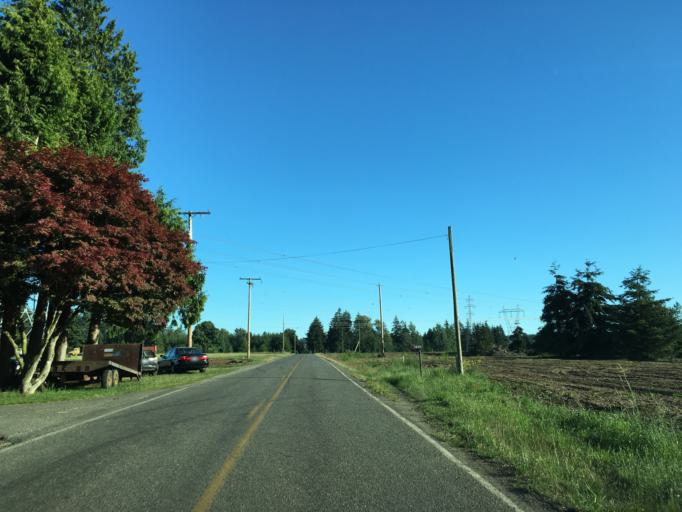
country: US
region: Washington
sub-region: Whatcom County
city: Ferndale
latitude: 48.9115
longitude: -122.6165
